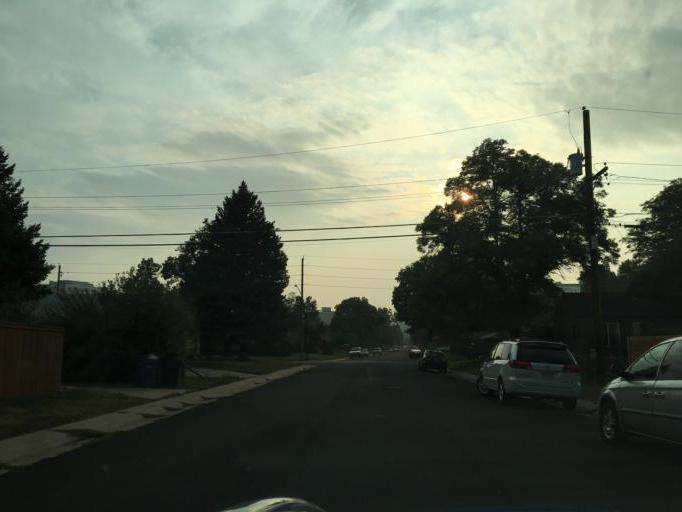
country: US
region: Colorado
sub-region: Arapahoe County
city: Glendale
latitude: 39.6843
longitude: -104.9308
